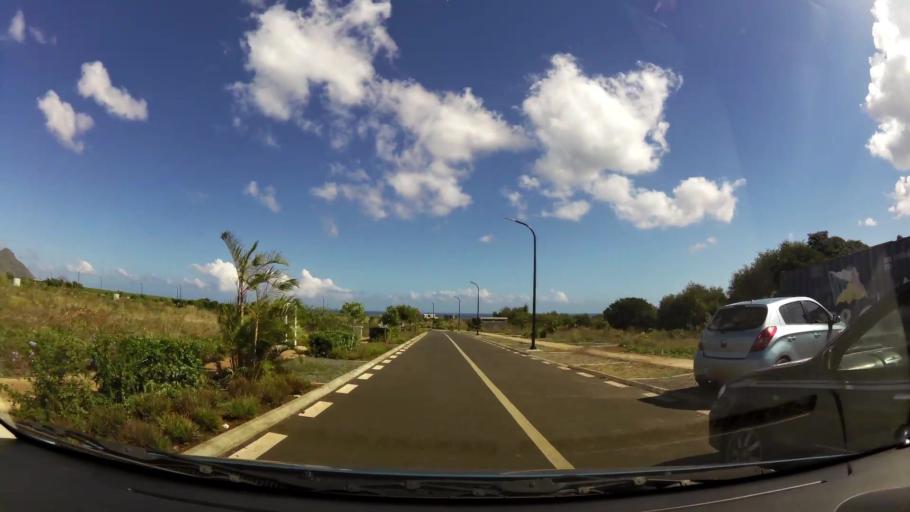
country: MU
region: Black River
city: Cascavelle
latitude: -20.2817
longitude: 57.3907
